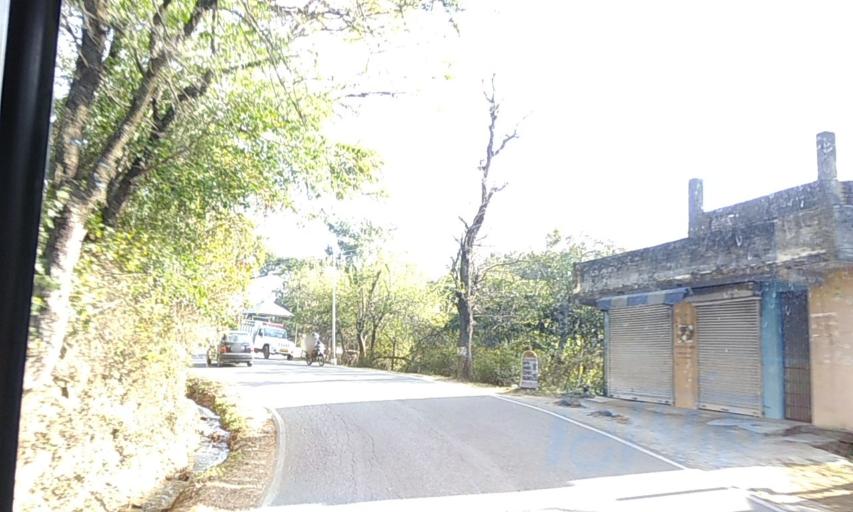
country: IN
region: Himachal Pradesh
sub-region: Kangra
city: Palampur
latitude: 32.0838
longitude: 76.5217
